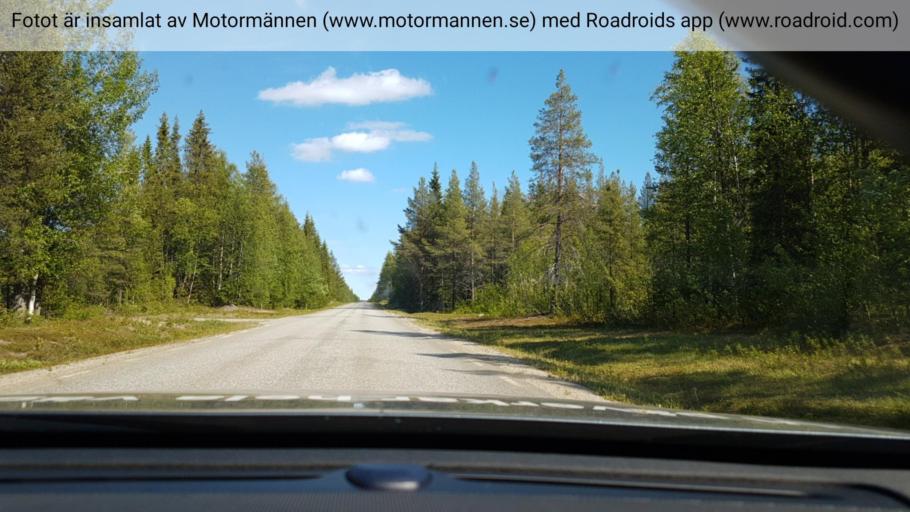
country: SE
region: Vaesterbotten
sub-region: Lycksele Kommun
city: Soderfors
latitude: 64.6338
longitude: 17.9328
